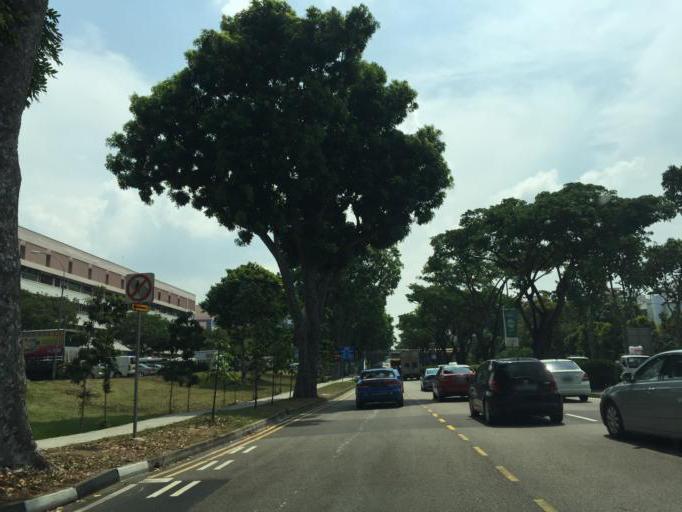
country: SG
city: Singapore
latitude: 1.3356
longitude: 103.9519
